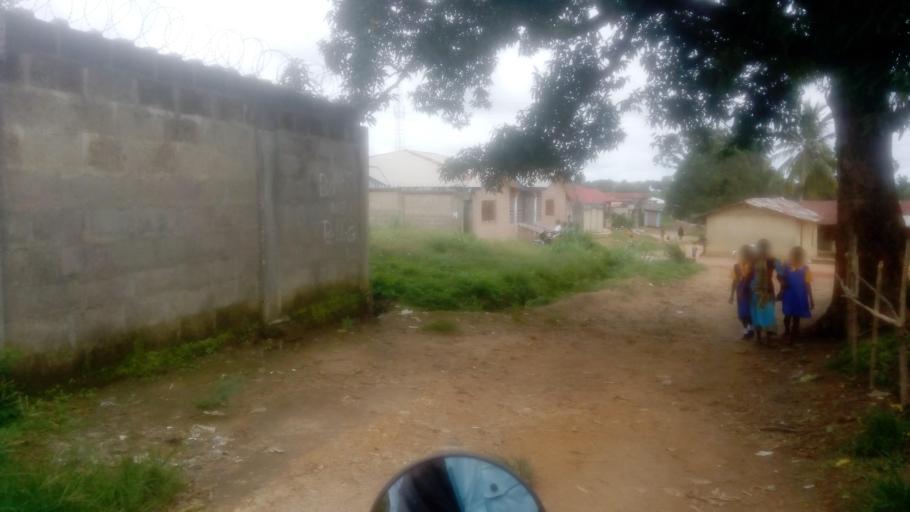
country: SL
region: Southern Province
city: Bo
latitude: 7.9414
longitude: -11.7303
